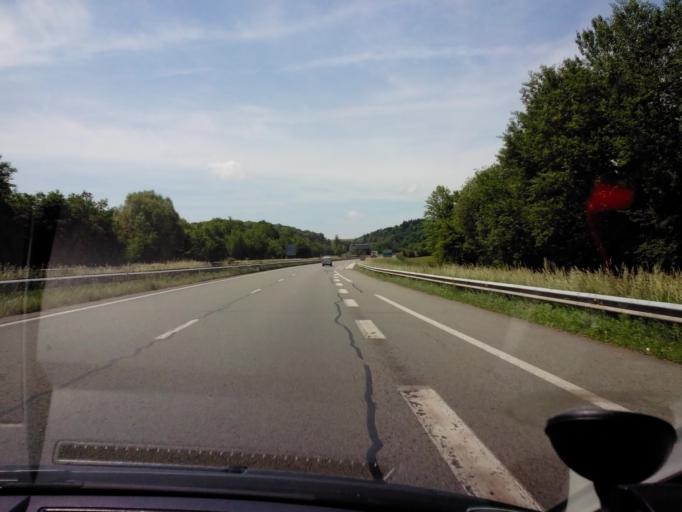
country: FR
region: Champagne-Ardenne
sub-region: Departement de la Haute-Marne
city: Avrecourt
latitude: 47.9719
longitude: 5.4948
